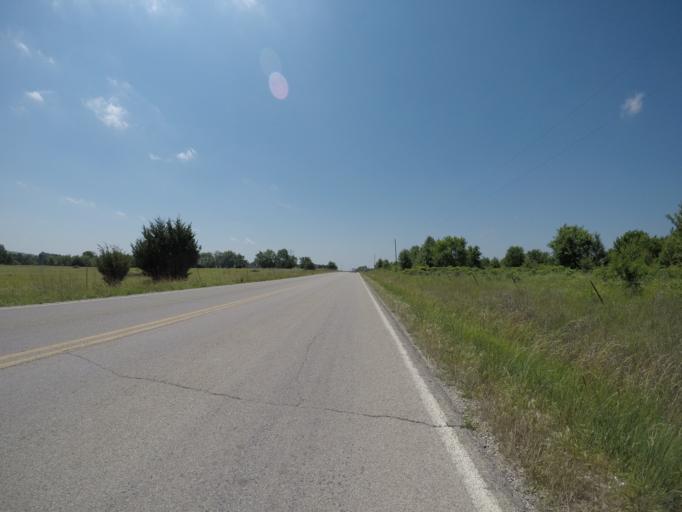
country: US
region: Kansas
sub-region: Pottawatomie County
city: Westmoreland
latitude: 39.3145
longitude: -96.4362
